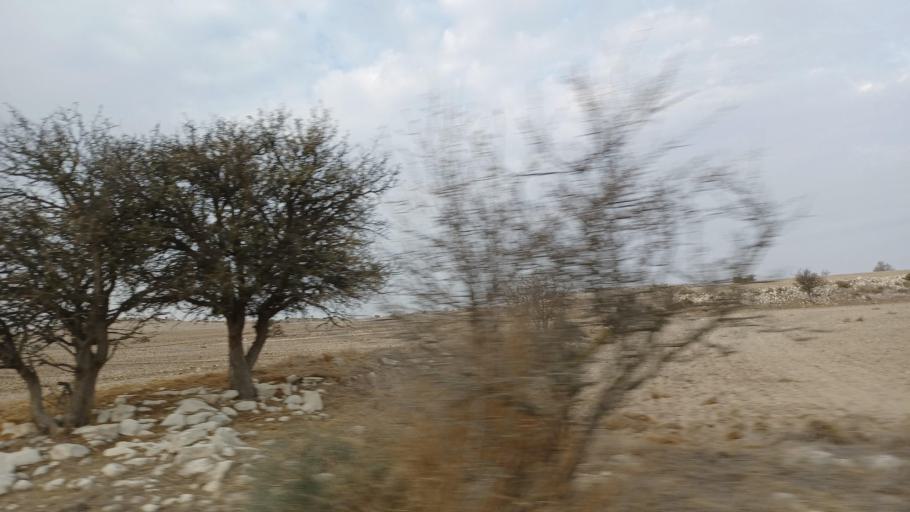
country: CY
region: Larnaka
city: Athienou
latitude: 35.0341
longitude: 33.5724
